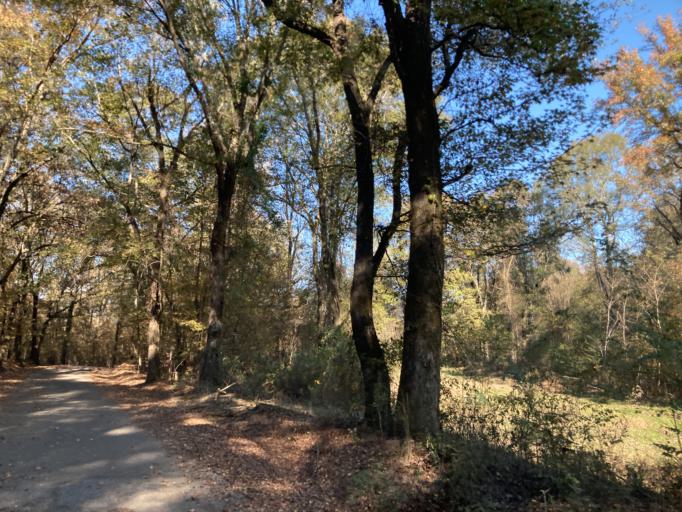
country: US
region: Mississippi
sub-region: Yazoo County
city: Yazoo City
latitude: 32.7610
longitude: -90.2786
